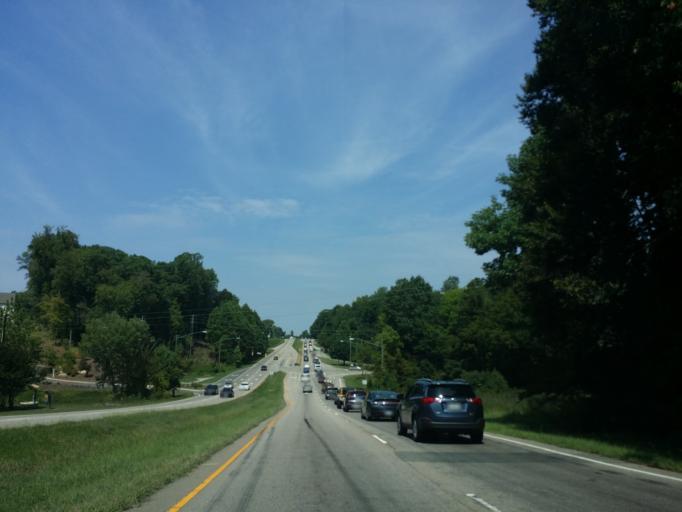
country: US
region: North Carolina
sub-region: Wake County
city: Cary
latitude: 35.8696
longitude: -78.7218
